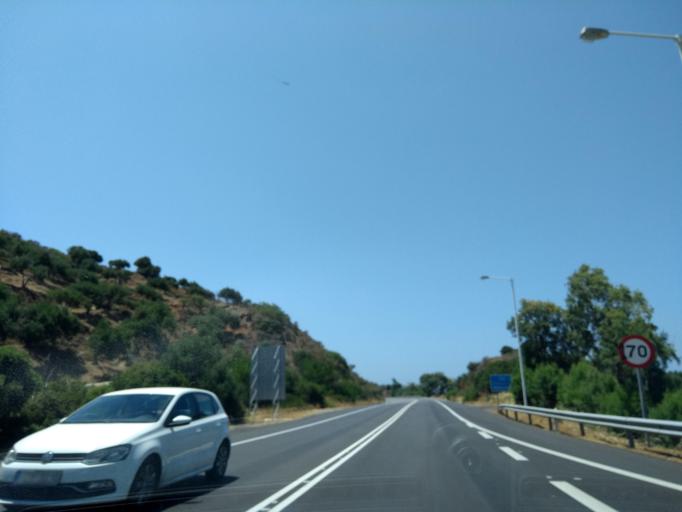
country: GR
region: Crete
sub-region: Nomos Irakleiou
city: Gazi
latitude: 35.3988
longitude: 25.0126
